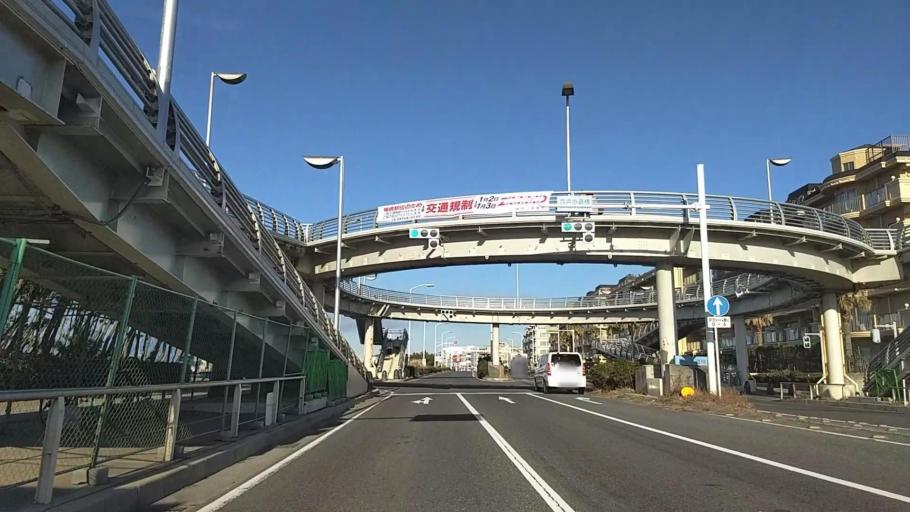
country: JP
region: Kanagawa
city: Fujisawa
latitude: 35.3111
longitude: 139.4788
